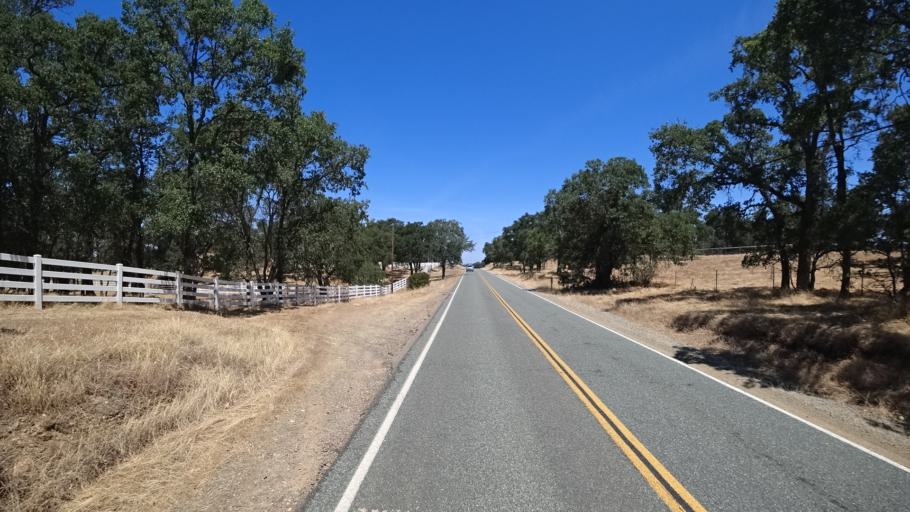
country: US
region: California
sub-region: Calaveras County
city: Valley Springs
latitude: 38.2031
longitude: -120.9052
